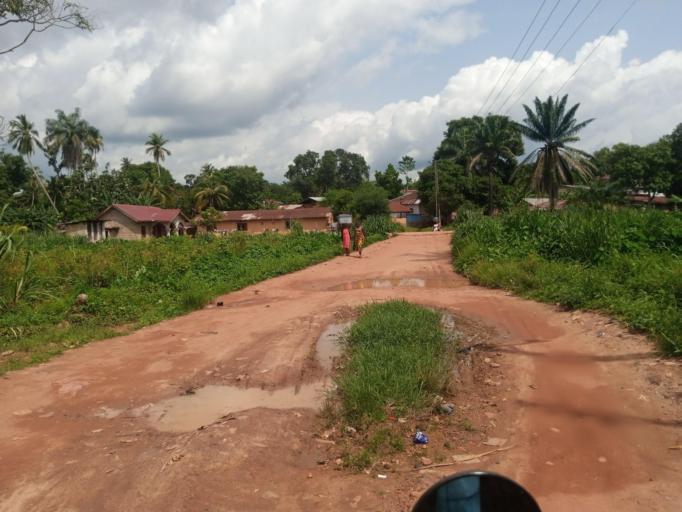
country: SL
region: Southern Province
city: Bo
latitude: 7.9747
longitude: -11.7342
